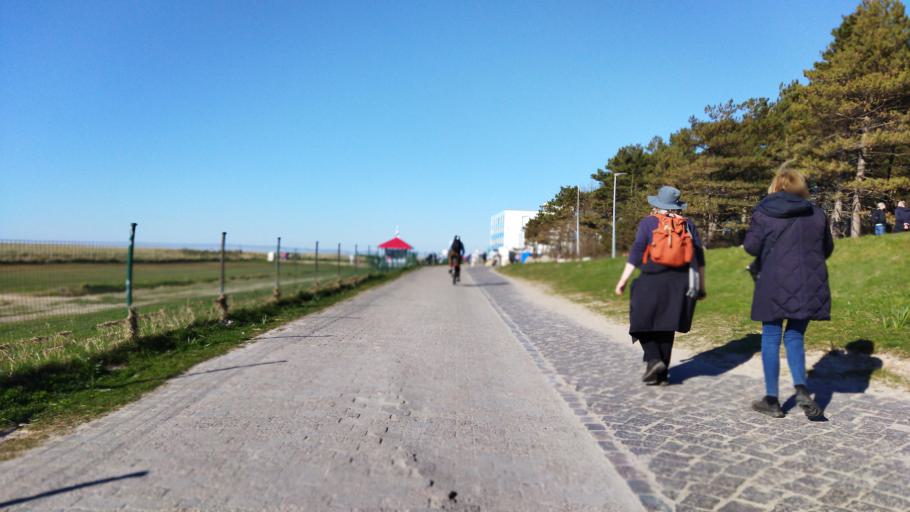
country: DE
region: Lower Saxony
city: Nordholz
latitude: 53.8582
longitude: 8.5894
